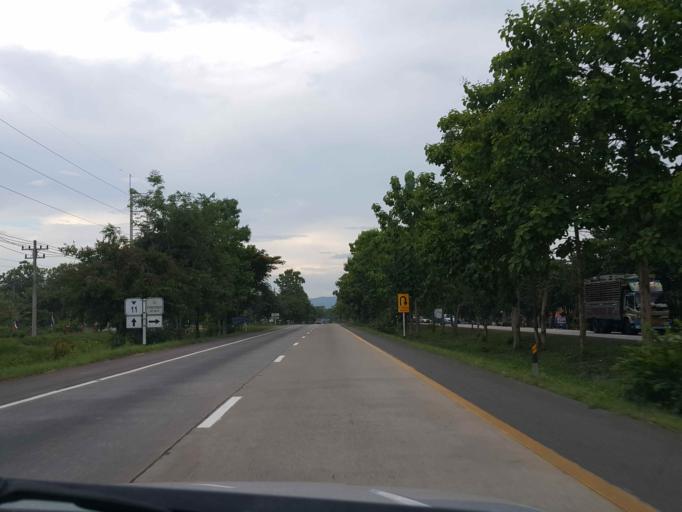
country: TH
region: Lampang
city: Hang Chat
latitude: 18.3201
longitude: 99.3252
